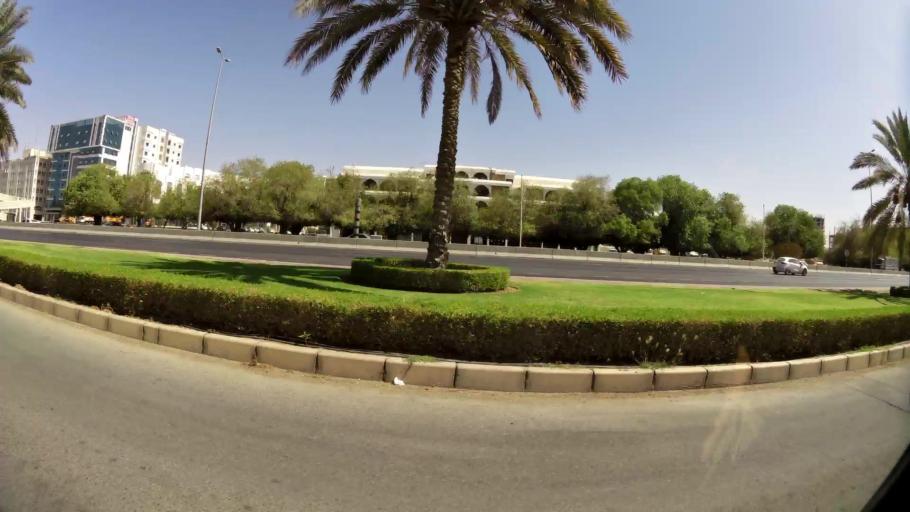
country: OM
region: Muhafazat Masqat
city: Bawshar
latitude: 23.5892
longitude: 58.3623
